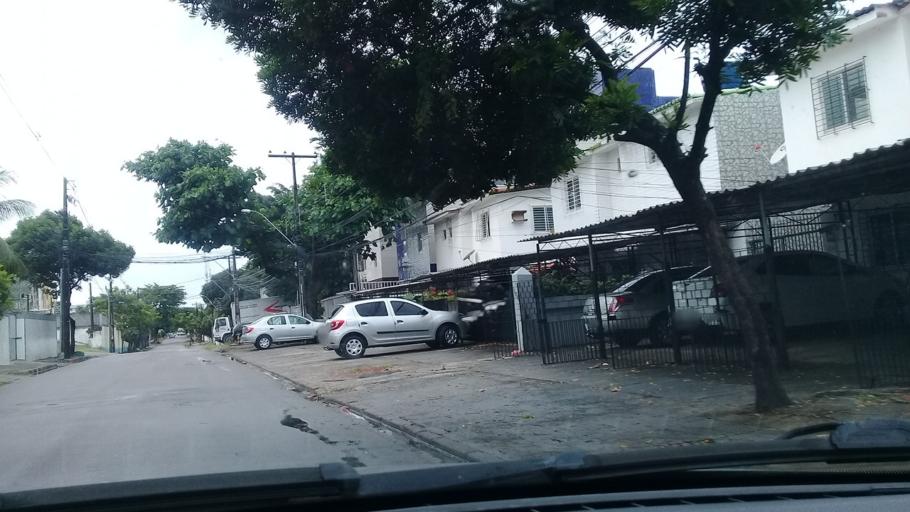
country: BR
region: Pernambuco
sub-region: Jaboatao Dos Guararapes
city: Jaboatao
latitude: -8.1426
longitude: -34.9153
